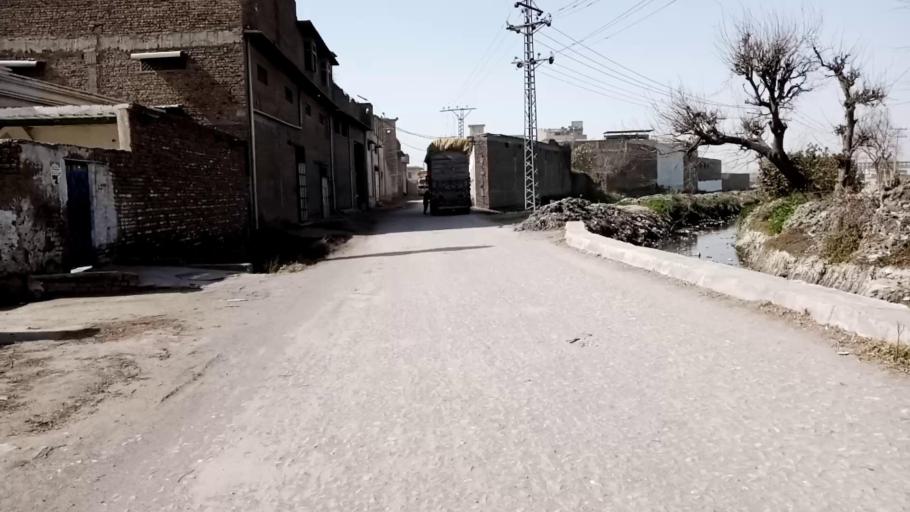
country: PK
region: Khyber Pakhtunkhwa
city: Peshawar
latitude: 34.0173
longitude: 71.6405
